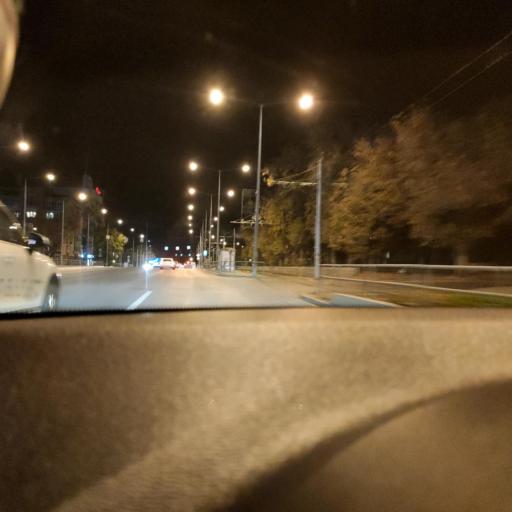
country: RU
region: Samara
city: Samara
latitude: 53.2188
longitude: 50.1539
